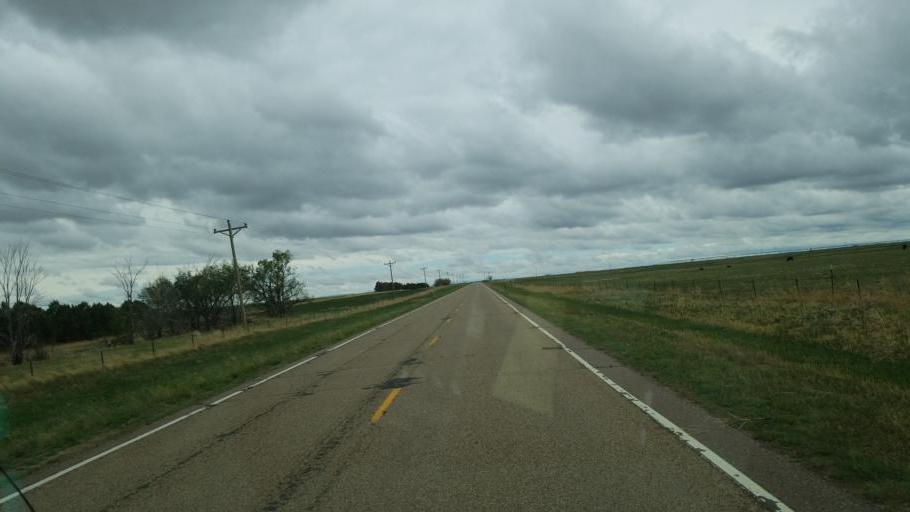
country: US
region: Colorado
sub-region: El Paso County
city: Ellicott
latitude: 38.8396
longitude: -103.9708
